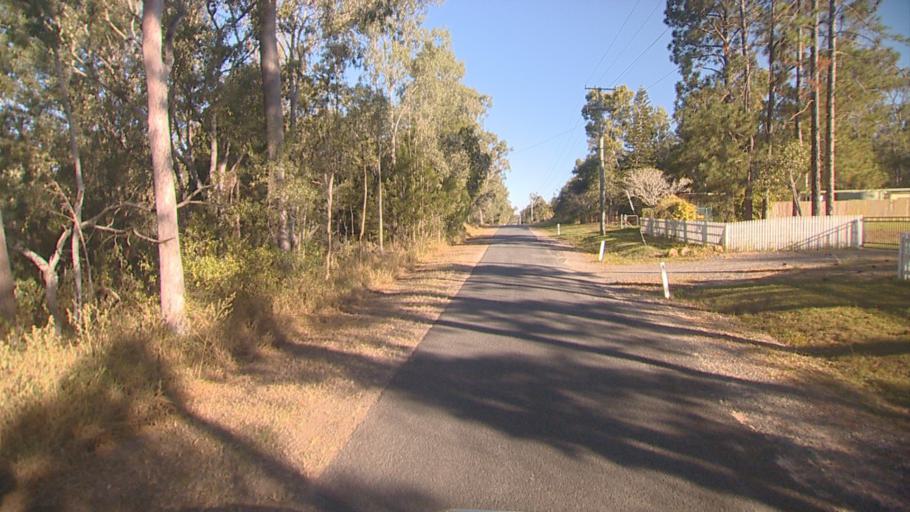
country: AU
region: Queensland
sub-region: Logan
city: North Maclean
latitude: -27.7809
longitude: 153.0399
